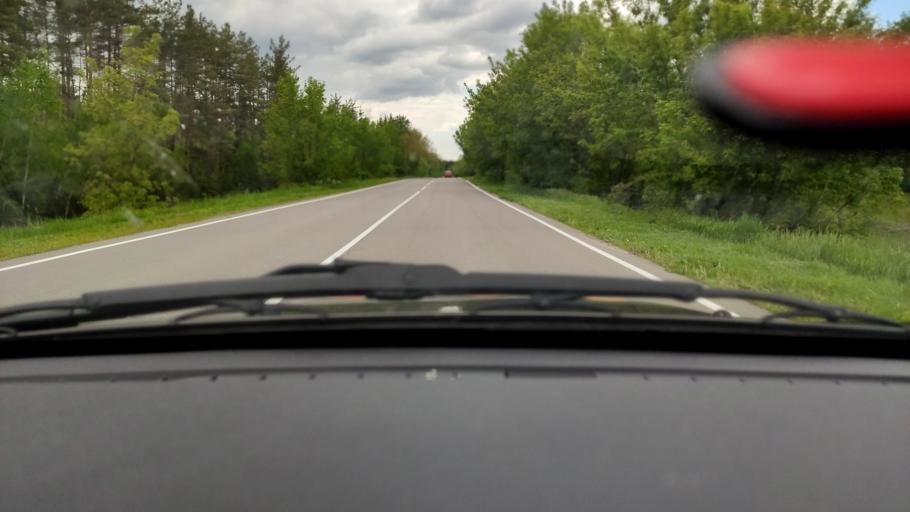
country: RU
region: Belgorod
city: Krasnoye
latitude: 51.0566
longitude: 38.8602
